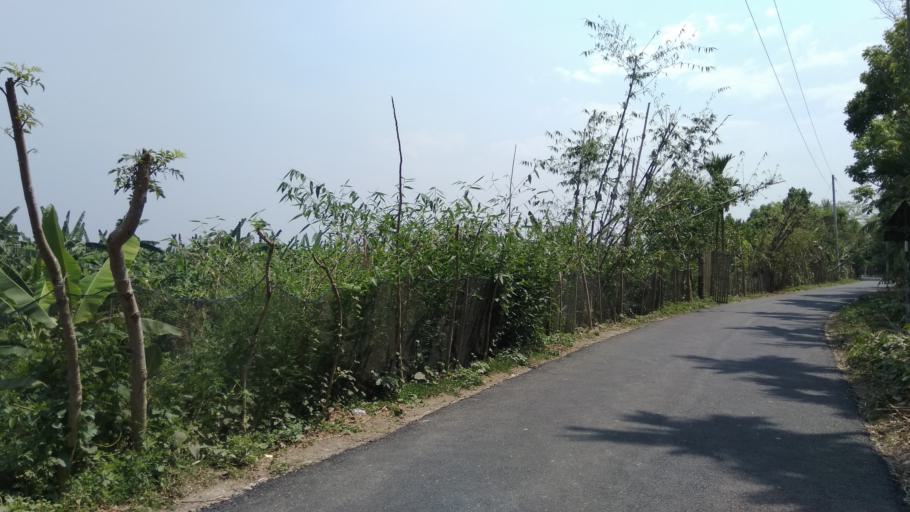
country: BD
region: Barisal
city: Mehendiganj
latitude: 22.9275
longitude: 90.3910
